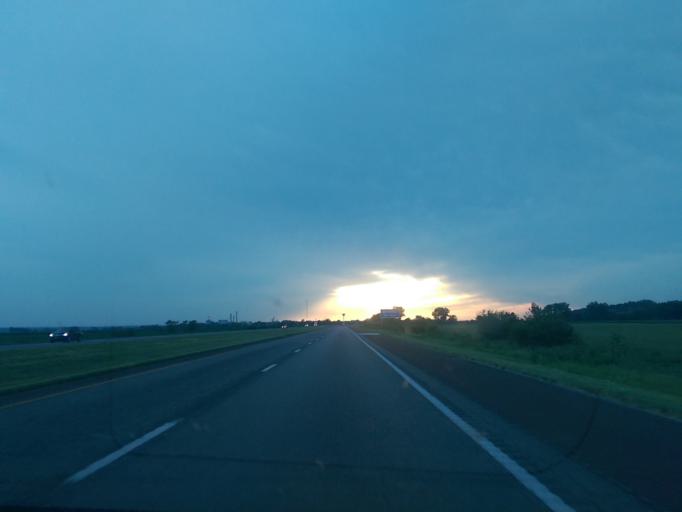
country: US
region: Missouri
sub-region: Holt County
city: Mound City
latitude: 40.1871
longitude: -95.3434
